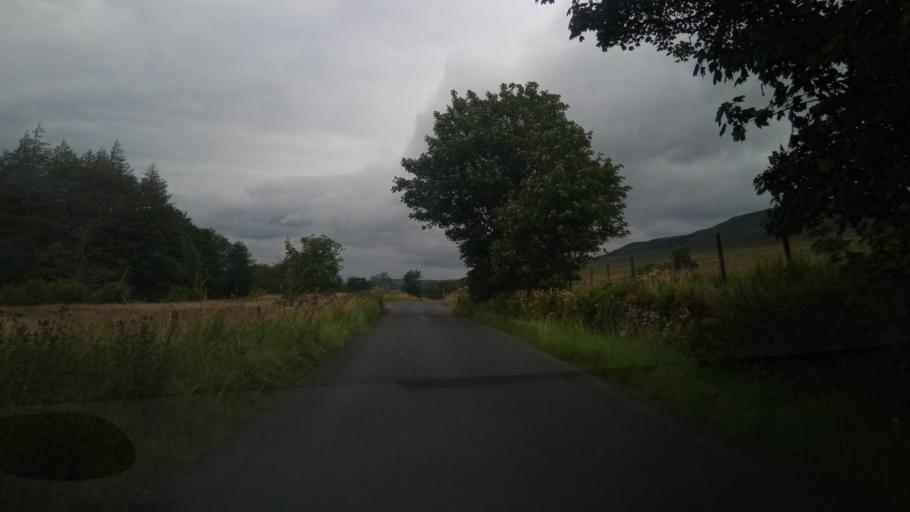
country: GB
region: England
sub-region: Cumbria
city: Kirkby Stephen
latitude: 54.3901
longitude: -2.3370
